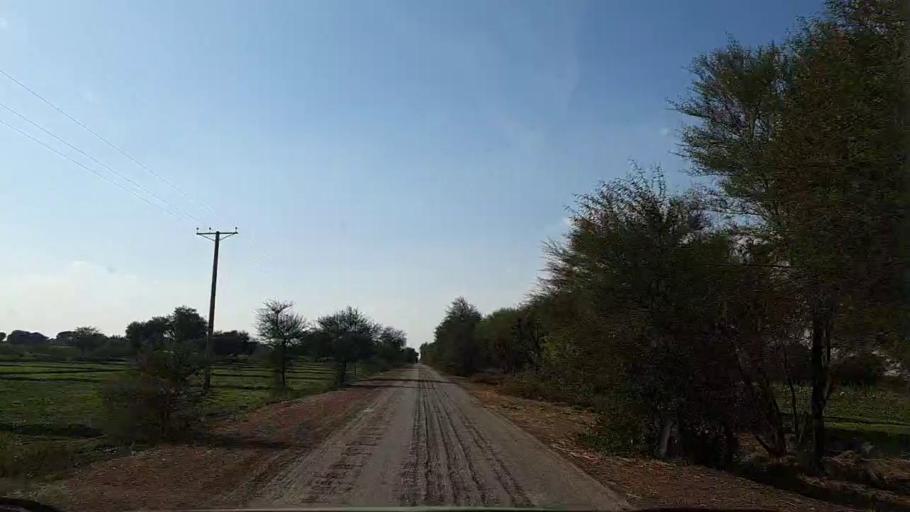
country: PK
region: Sindh
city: Pithoro
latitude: 25.6480
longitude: 69.3165
